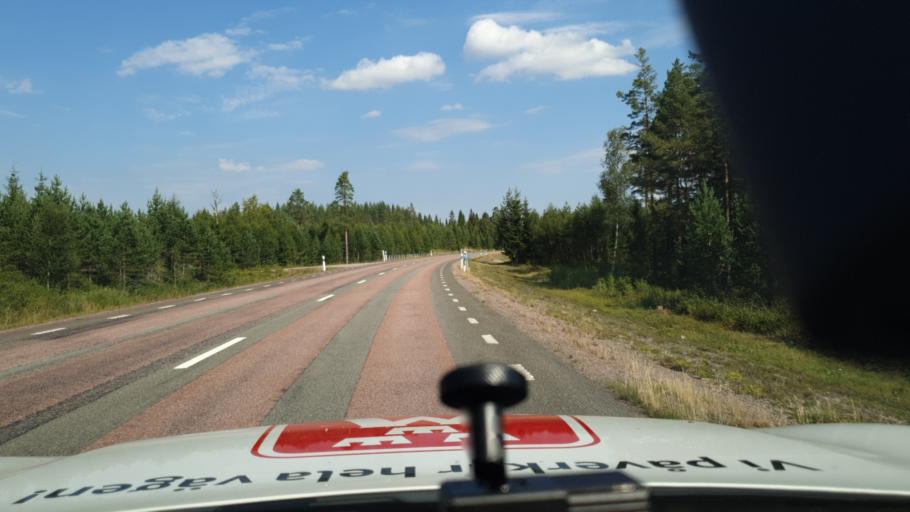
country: SE
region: Dalarna
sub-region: Malung-Saelens kommun
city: Malung
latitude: 60.5472
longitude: 13.5320
